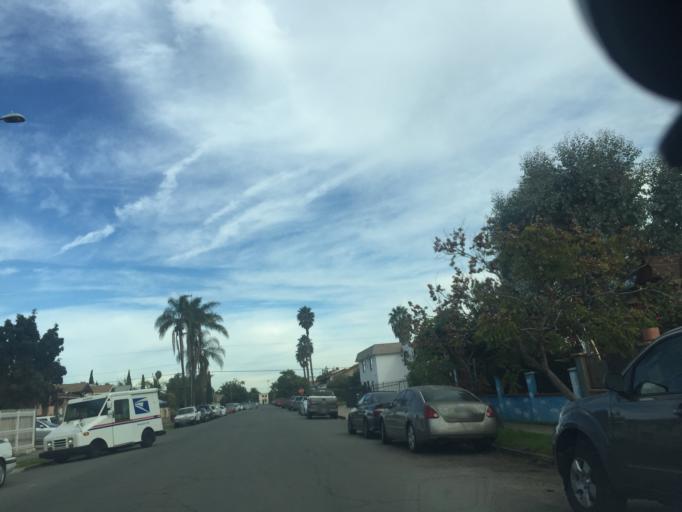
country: US
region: California
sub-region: San Diego County
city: Lemon Grove
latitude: 32.7506
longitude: -117.0987
